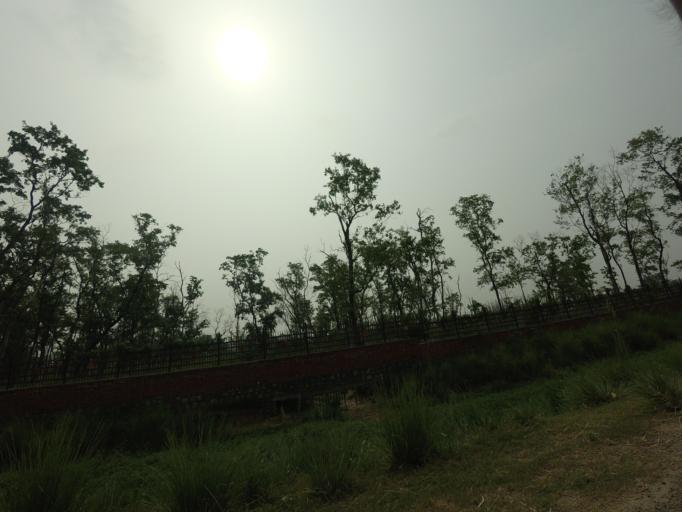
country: IN
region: Uttar Pradesh
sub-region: Maharajganj
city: Nautanwa
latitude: 27.4847
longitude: 83.2680
